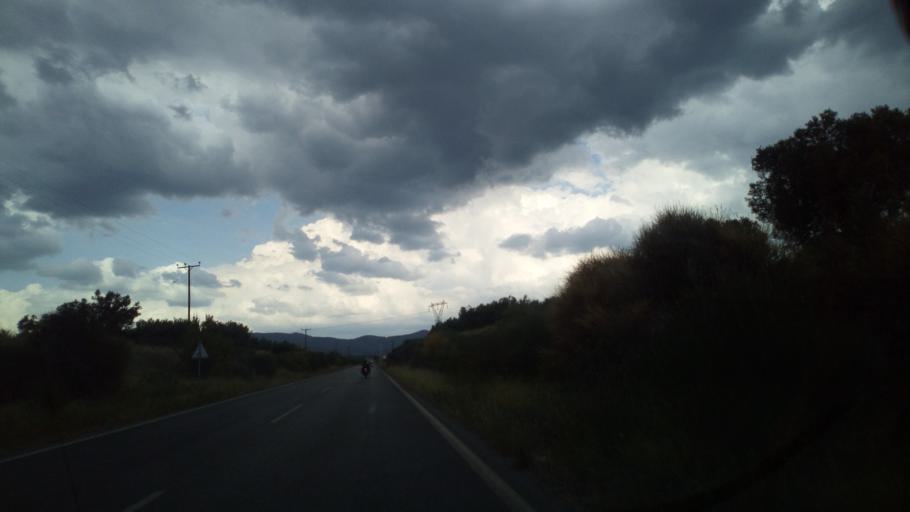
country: GR
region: Central Macedonia
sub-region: Nomos Chalkidikis
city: Kalyves Polygyrou
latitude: 40.3102
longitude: 23.4402
